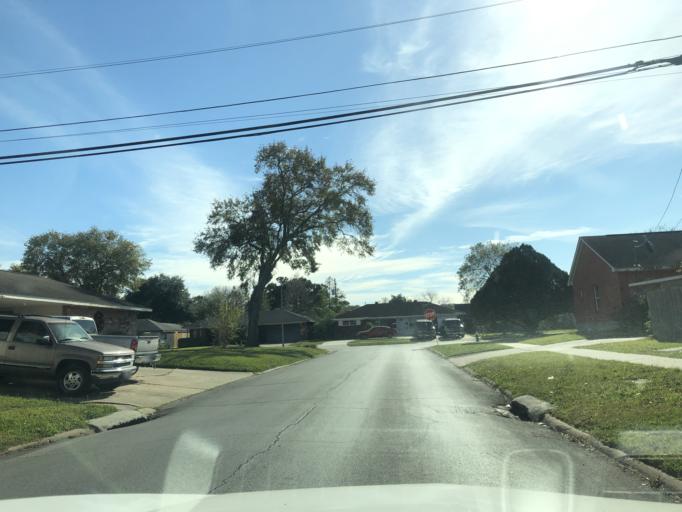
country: US
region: Texas
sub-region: Harris County
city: Bellaire
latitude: 29.6857
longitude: -95.5075
